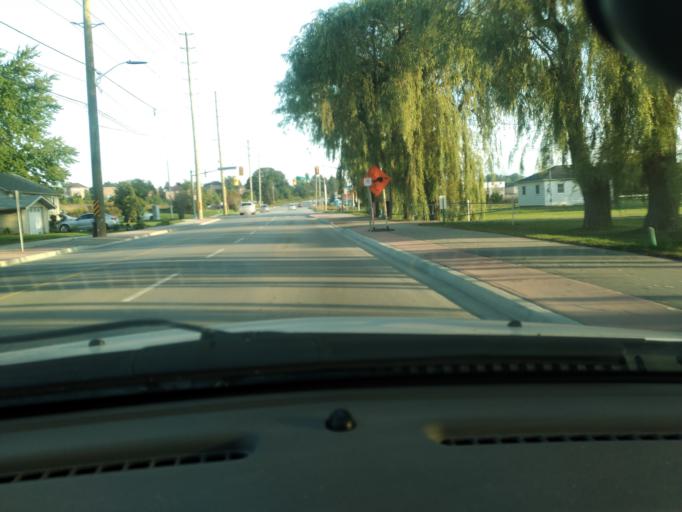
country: CA
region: Ontario
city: Bradford West Gwillimbury
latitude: 44.0995
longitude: -79.5688
